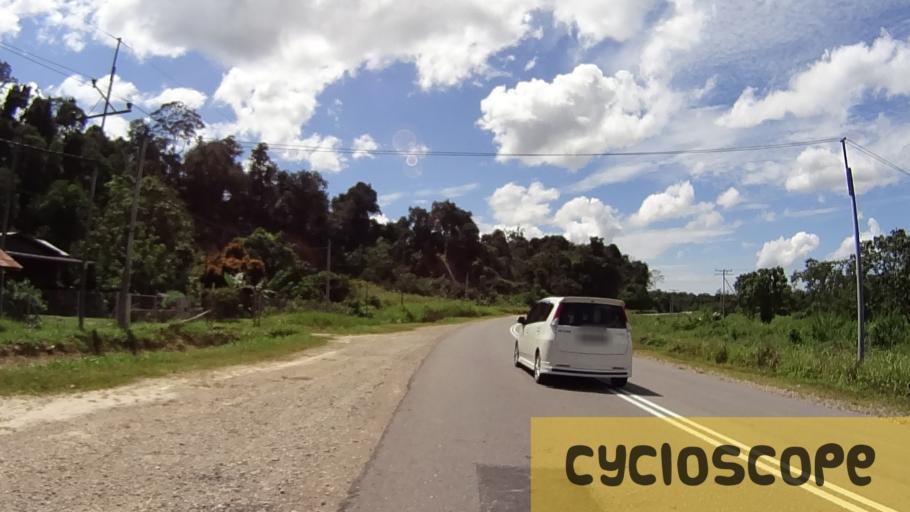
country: MY
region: Sabah
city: Beaufort
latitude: 5.2199
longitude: 115.6436
